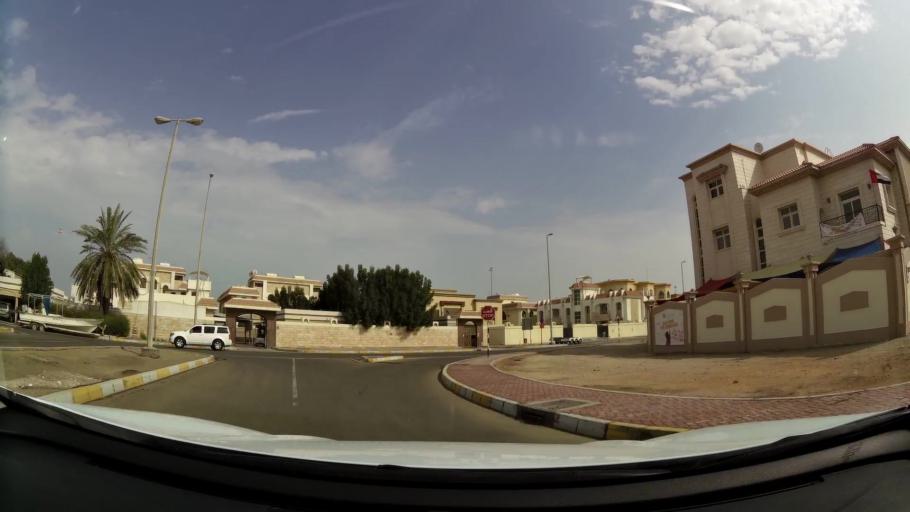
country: AE
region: Abu Dhabi
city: Abu Dhabi
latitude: 24.4422
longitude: 54.4248
